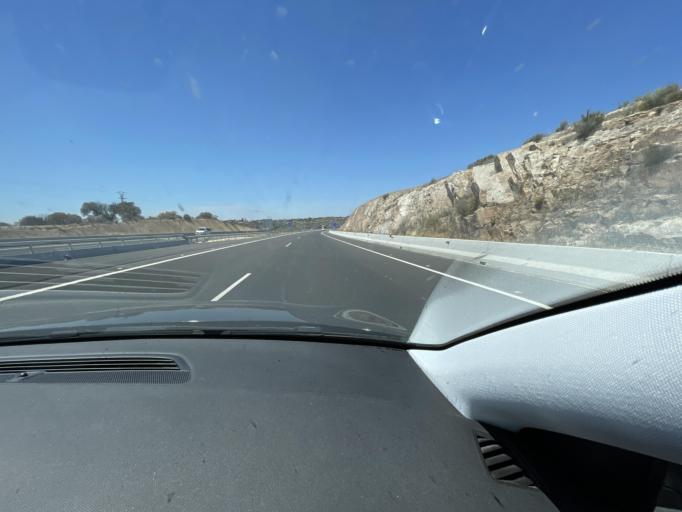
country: ES
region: Castille and Leon
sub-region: Provincia de Salamanca
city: Fuentes de Onoro
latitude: 40.5949
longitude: -6.8041
